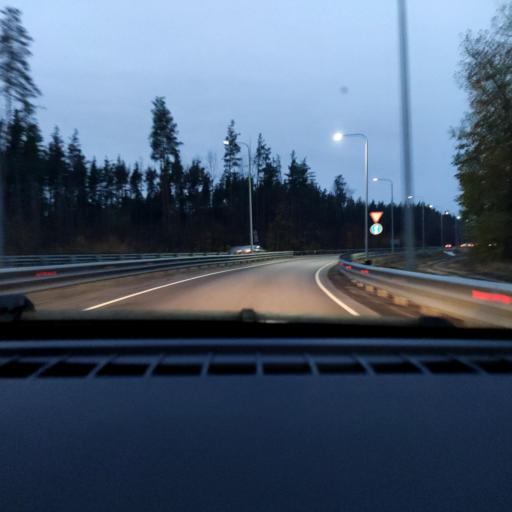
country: RU
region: Voronezj
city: Somovo
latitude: 51.6912
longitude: 39.2999
